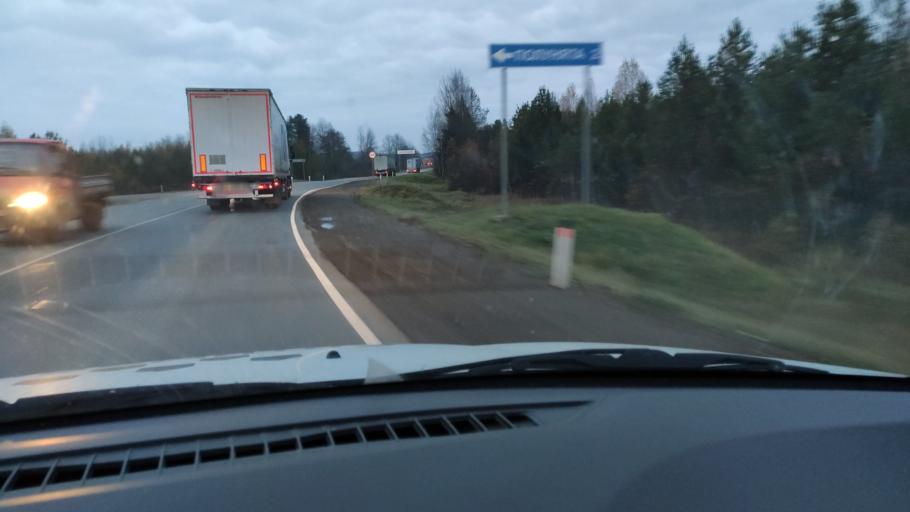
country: RU
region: Kirov
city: Kostino
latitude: 58.8544
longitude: 53.2112
